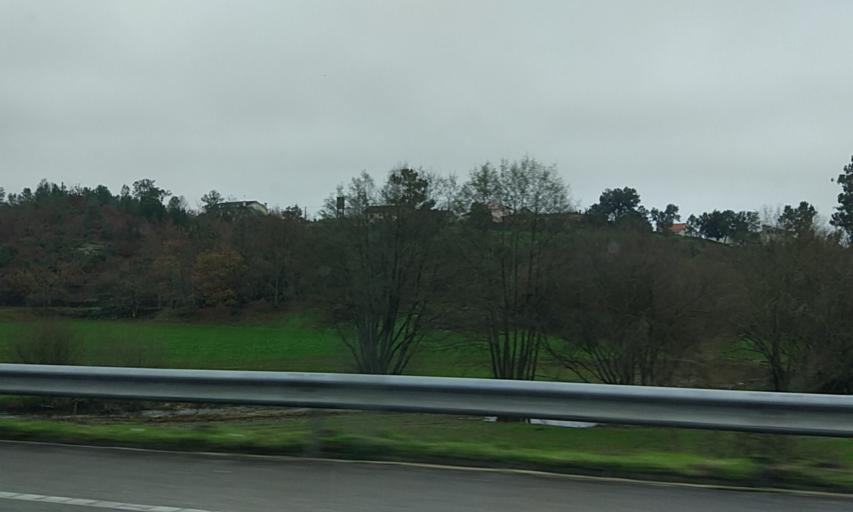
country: PT
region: Viseu
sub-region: Concelho de Tondela
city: Tondela
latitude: 40.5782
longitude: -8.0263
